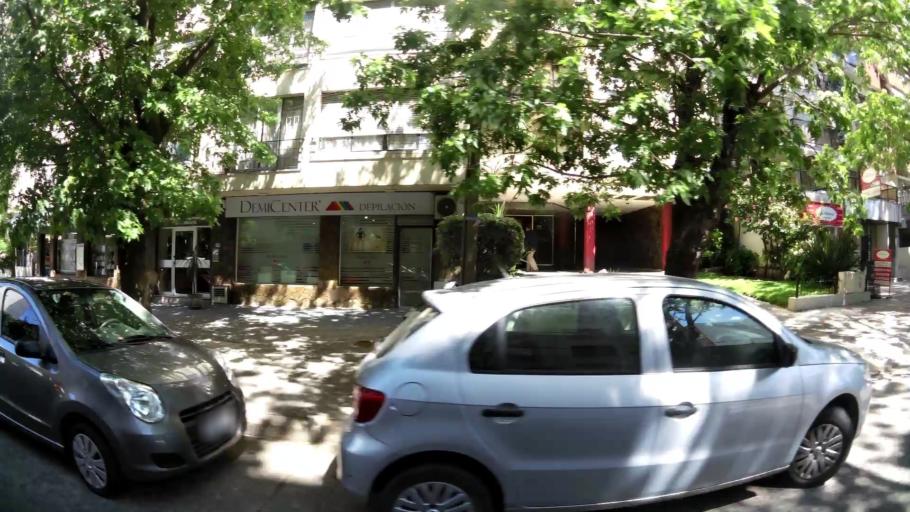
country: UY
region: Montevideo
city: Montevideo
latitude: -34.9087
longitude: -56.1477
